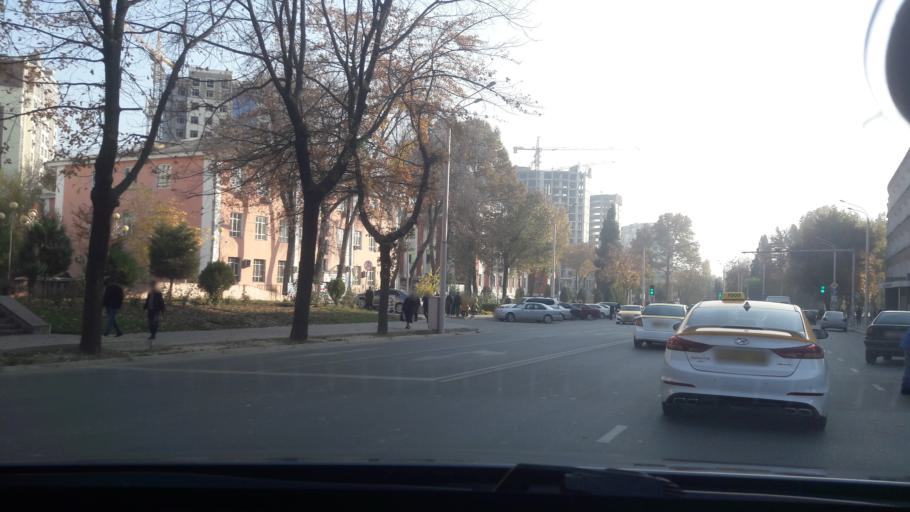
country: TJ
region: Dushanbe
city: Dushanbe
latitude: 38.5758
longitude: 68.7936
